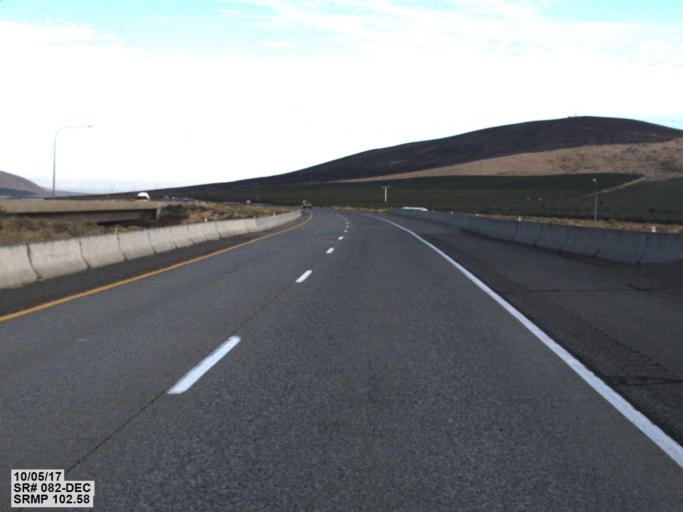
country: US
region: Washington
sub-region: Benton County
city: West Richland
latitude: 46.2437
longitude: -119.3617
